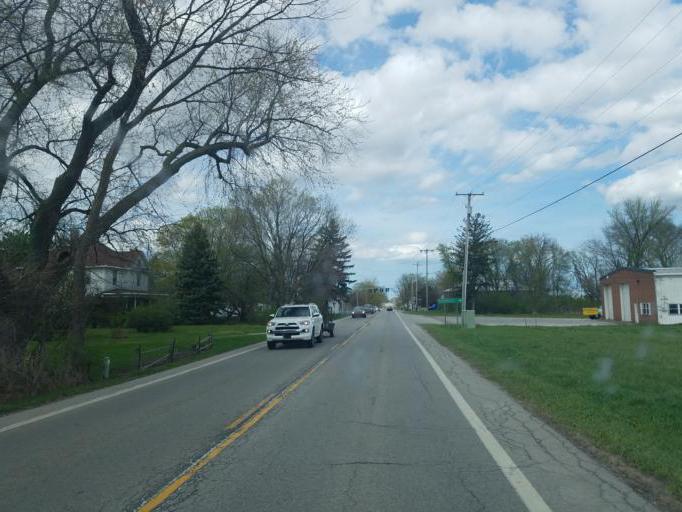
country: US
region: Ohio
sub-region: Erie County
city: Sandusky
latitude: 41.3597
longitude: -82.7501
